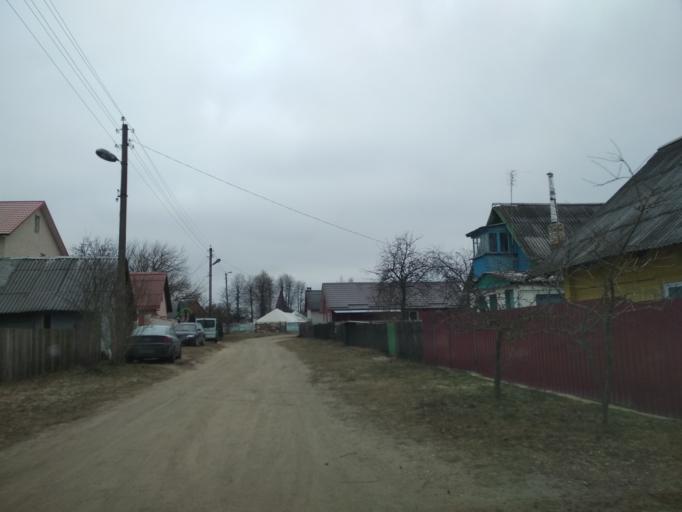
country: BY
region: Minsk
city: Mar''ina Horka
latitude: 53.5113
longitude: 28.1521
